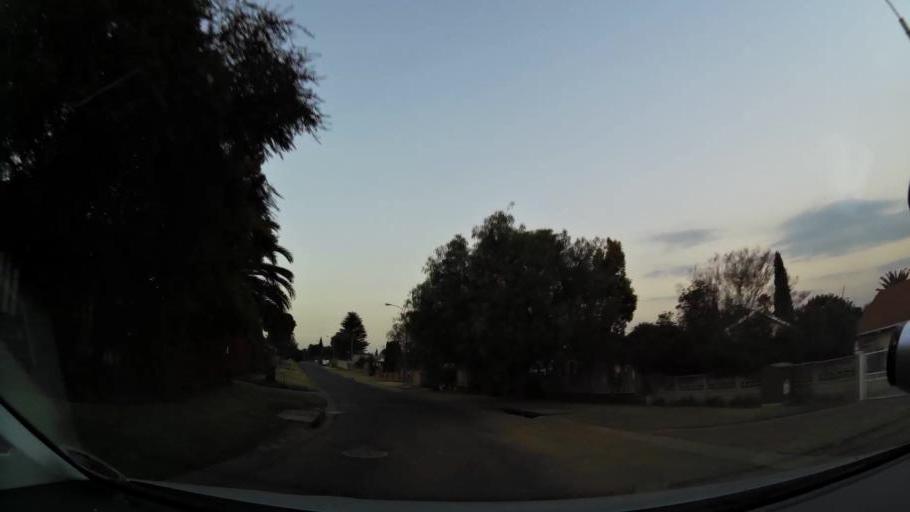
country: ZA
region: Gauteng
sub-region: Ekurhuleni Metropolitan Municipality
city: Tembisa
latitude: -26.0547
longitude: 28.2431
